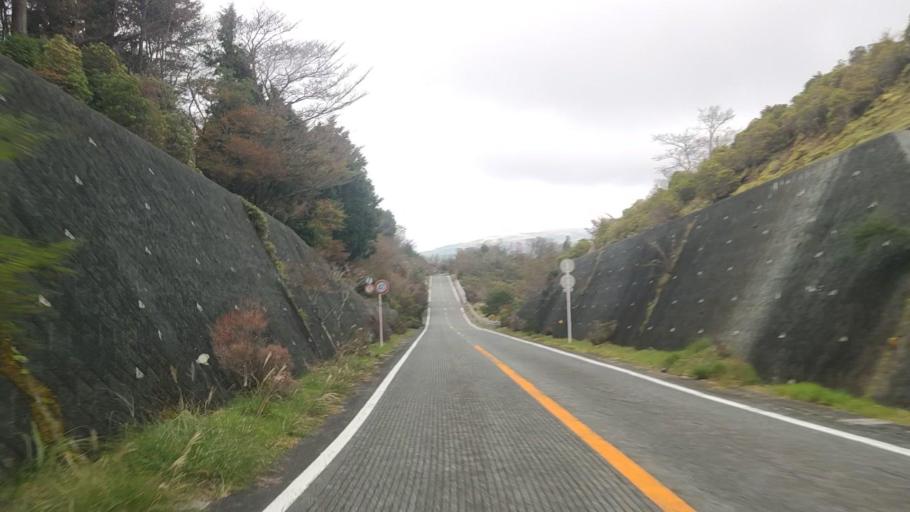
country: JP
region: Shizuoka
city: Heda
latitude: 34.8866
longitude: 138.8470
